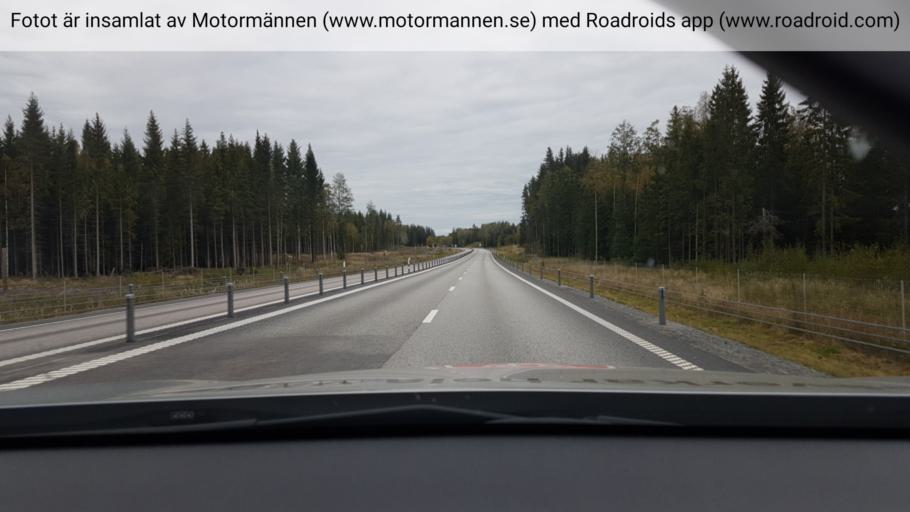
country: SE
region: Uppsala
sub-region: Heby Kommun
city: Heby
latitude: 60.0229
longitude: 16.8624
